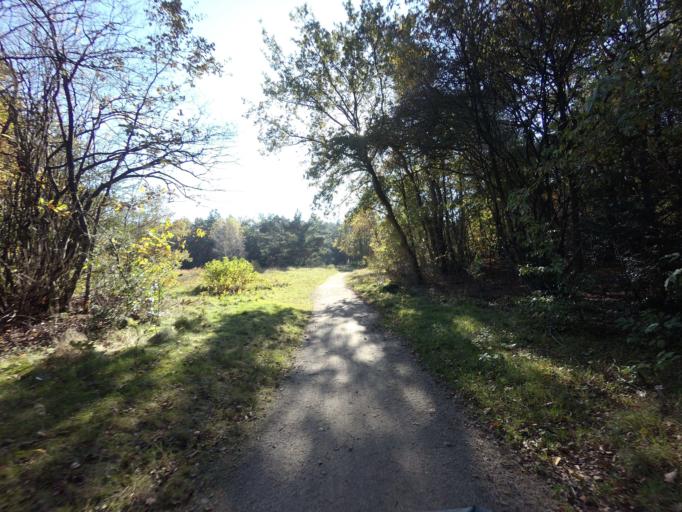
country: NL
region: North Holland
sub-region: Gemeente Laren
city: Laren
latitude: 52.2440
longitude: 5.2283
